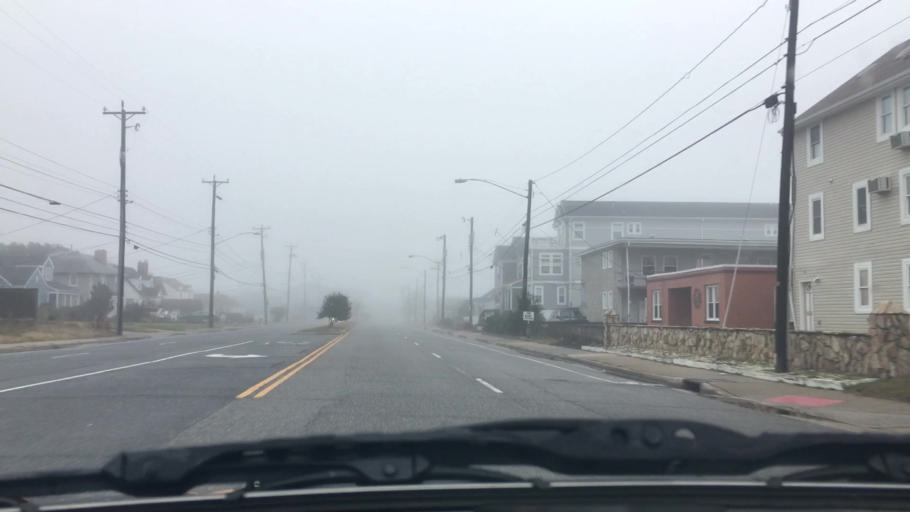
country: US
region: Virginia
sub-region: City of Hampton
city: East Hampton
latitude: 36.9670
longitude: -76.2814
